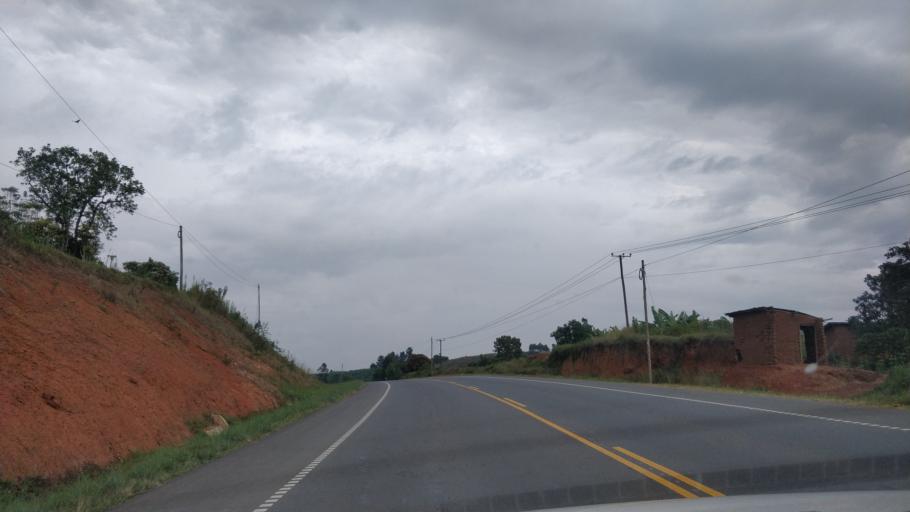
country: UG
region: Western Region
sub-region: Sheema District
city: Kibingo
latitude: -0.6554
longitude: 30.4808
